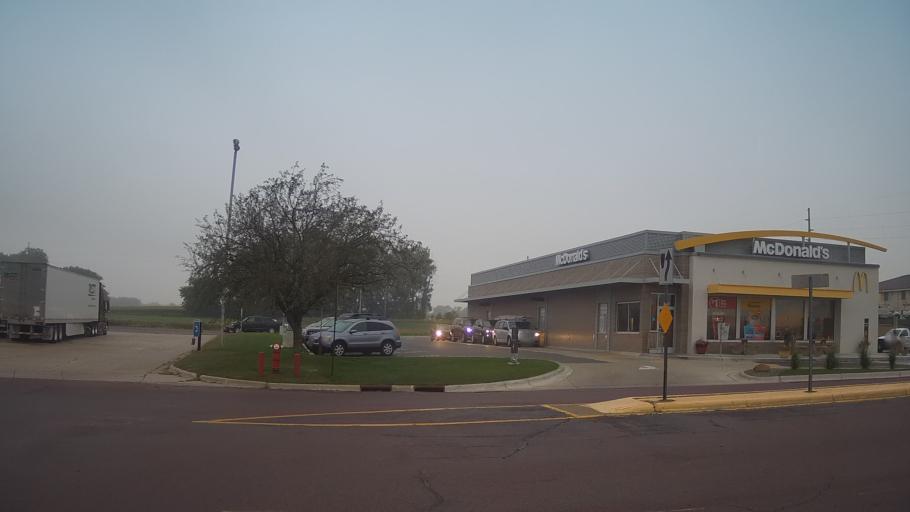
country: US
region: Minnesota
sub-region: Martin County
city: Fairmont
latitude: 43.6765
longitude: -94.4483
